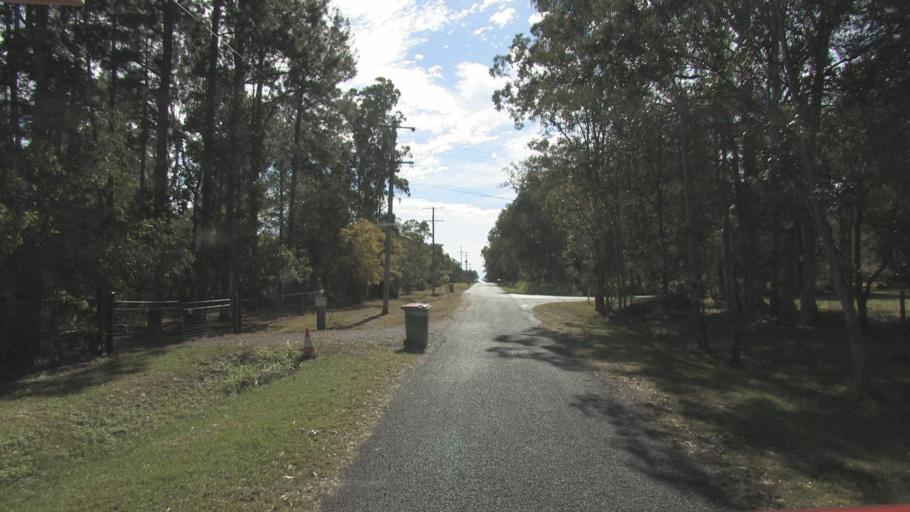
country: AU
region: Queensland
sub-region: Logan
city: North Maclean
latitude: -27.7800
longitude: 152.9905
